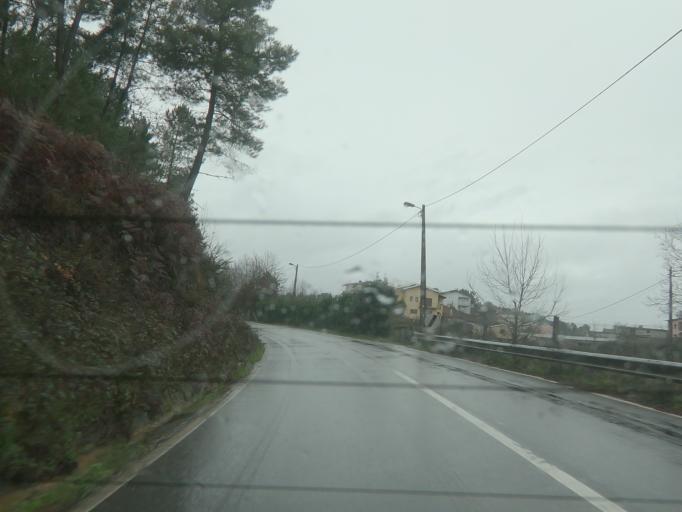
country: PT
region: Vila Real
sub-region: Vila Real
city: Vila Real
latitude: 41.2618
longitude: -7.6886
